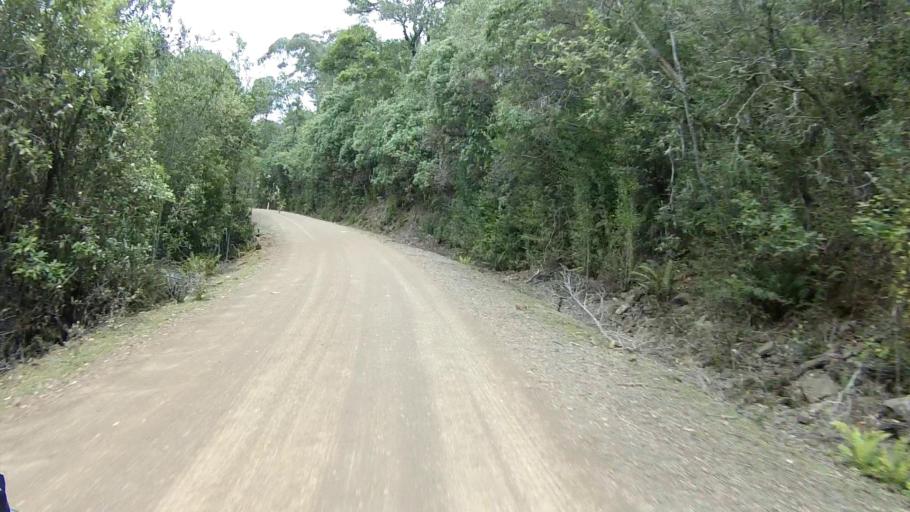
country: AU
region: Tasmania
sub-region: Sorell
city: Sorell
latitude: -42.6051
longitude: 147.8803
